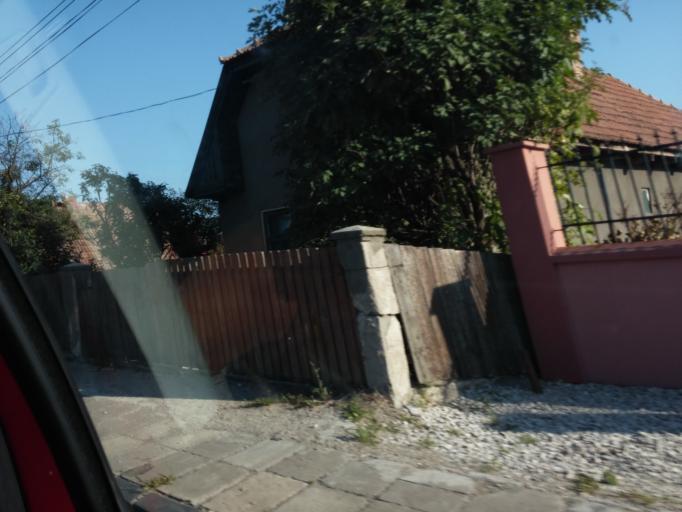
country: RO
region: Cluj
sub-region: Comuna Tureni
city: Tureni
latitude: 46.6318
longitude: 23.6993
